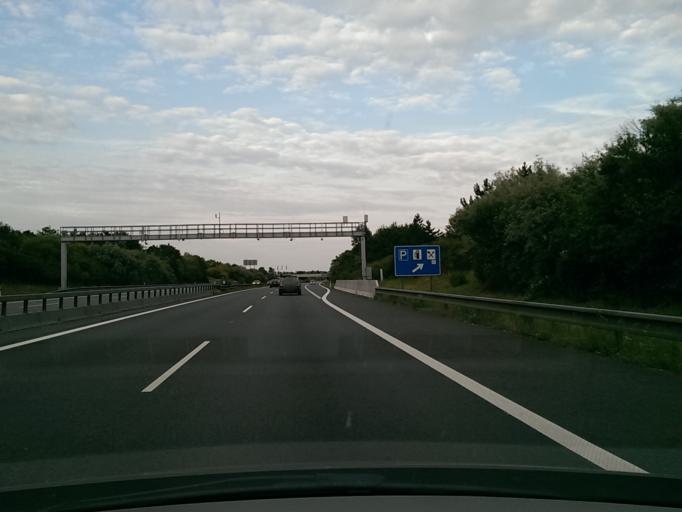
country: CZ
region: South Moravian
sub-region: Mesto Brno
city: Brno
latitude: 49.1629
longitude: 16.6543
